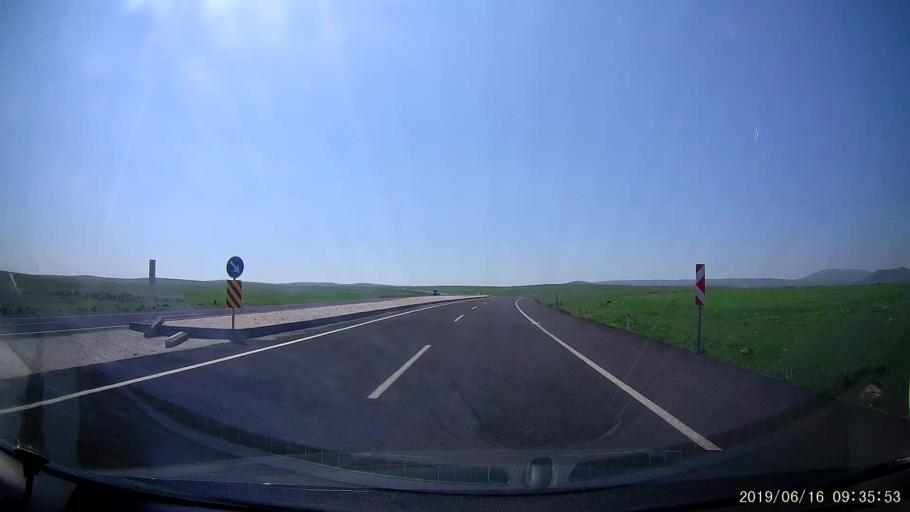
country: TR
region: Kars
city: Kars
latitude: 40.5644
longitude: 43.1637
